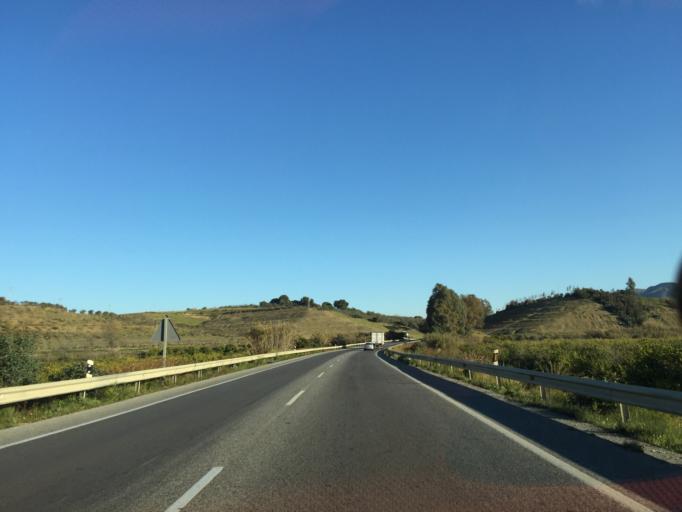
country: ES
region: Andalusia
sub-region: Provincia de Malaga
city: Pizarra
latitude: 36.7241
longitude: -4.7090
